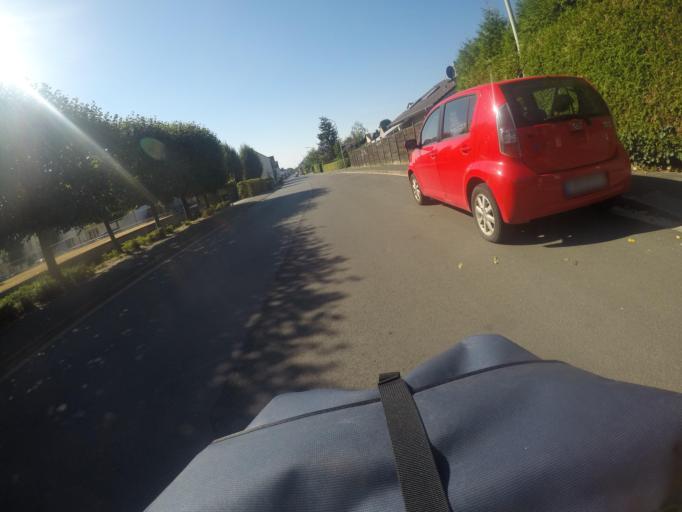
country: DE
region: North Rhine-Westphalia
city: Leichlingen
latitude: 51.1094
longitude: 6.9993
